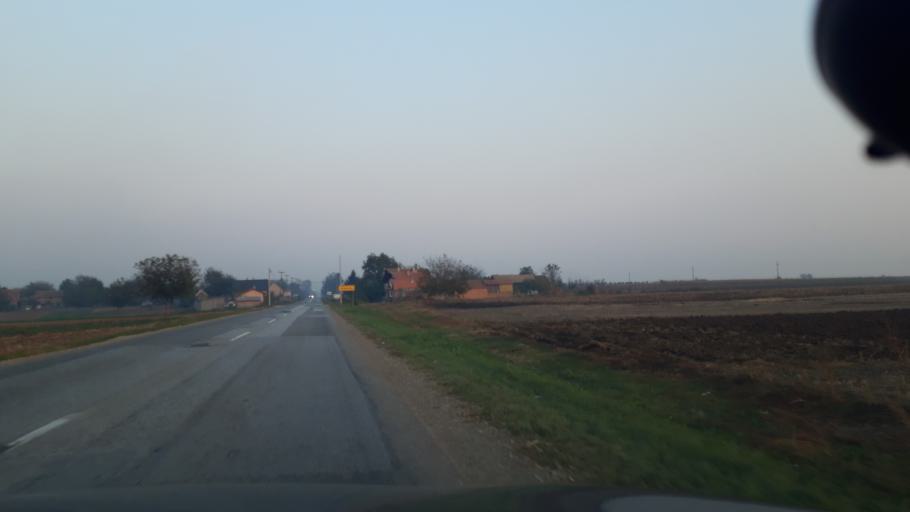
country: RS
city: Putinci
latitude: 45.0030
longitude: 19.9260
